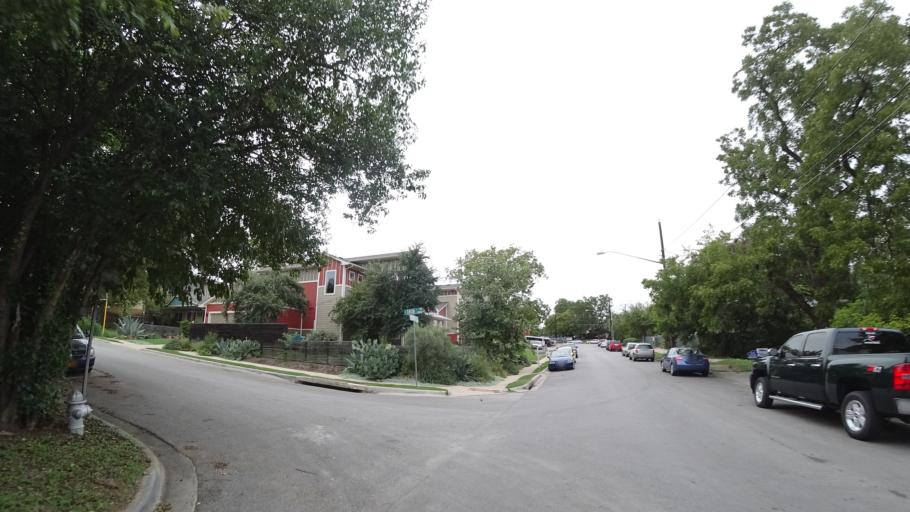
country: US
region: Texas
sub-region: Travis County
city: Austin
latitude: 30.2789
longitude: -97.7198
